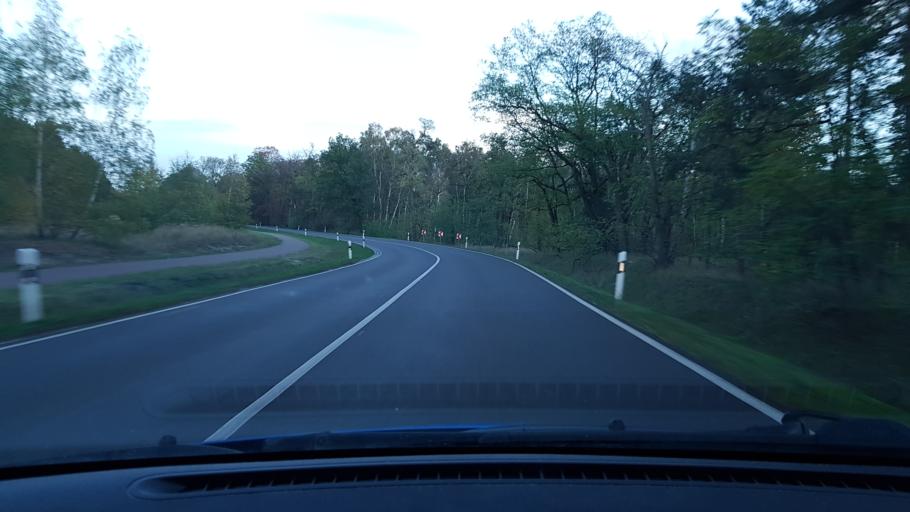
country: DE
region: Saxony-Anhalt
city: Wahlitz
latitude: 52.0917
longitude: 11.7920
